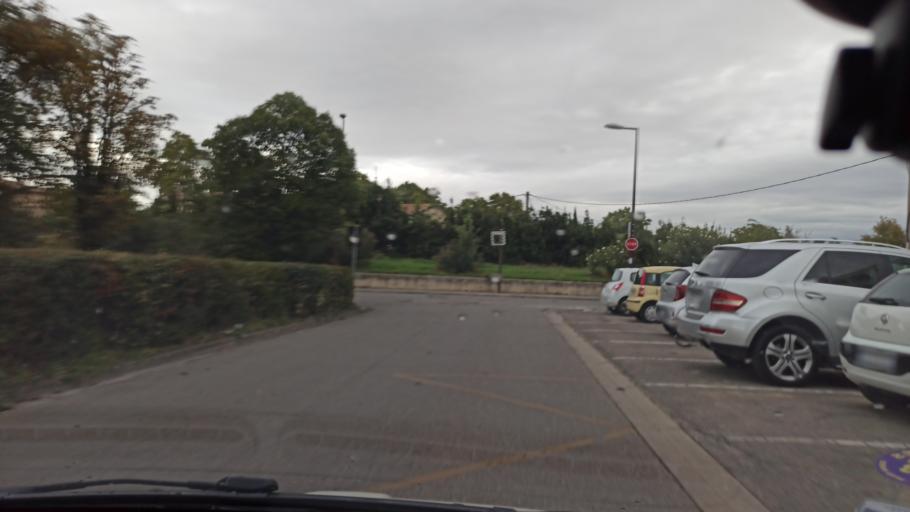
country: FR
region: Provence-Alpes-Cote d'Azur
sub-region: Departement du Vaucluse
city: Montfavet
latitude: 43.9417
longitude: 4.8758
